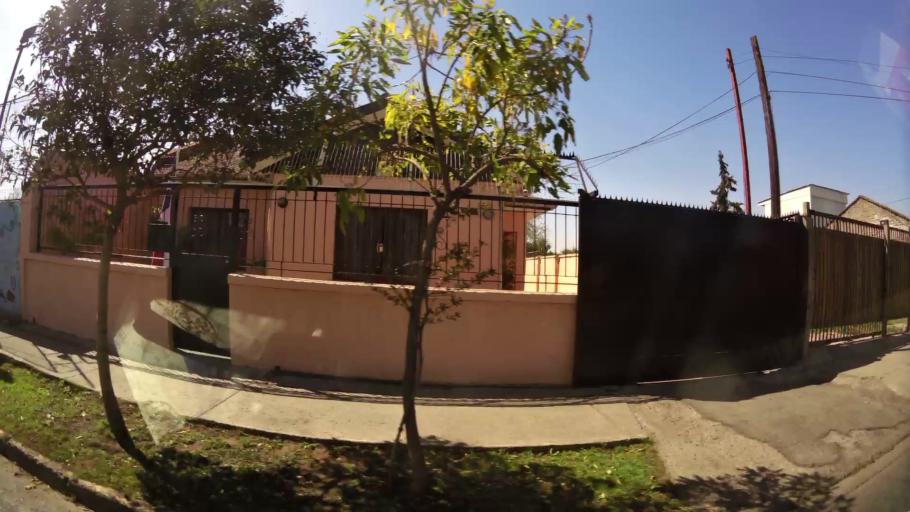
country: CL
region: Santiago Metropolitan
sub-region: Provincia de Santiago
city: Lo Prado
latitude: -33.4995
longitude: -70.7263
